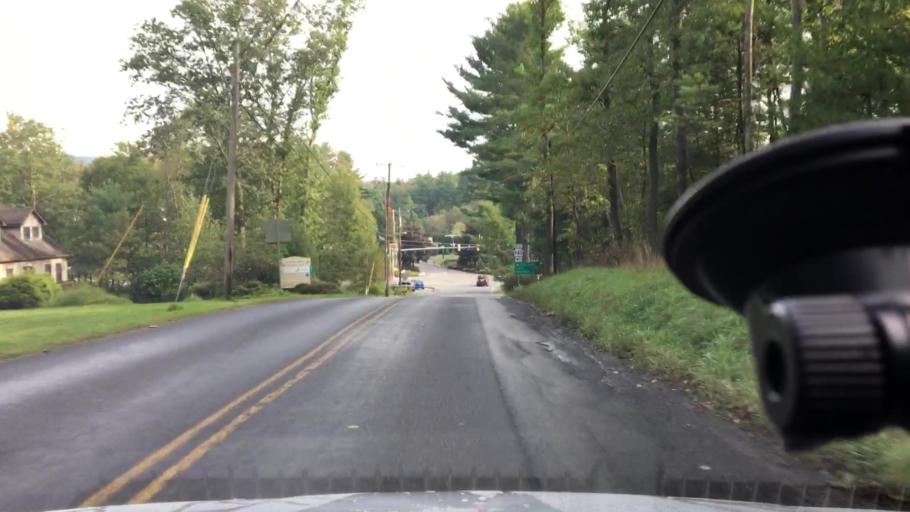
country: US
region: Pennsylvania
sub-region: Monroe County
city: Mount Pocono
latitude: 41.1261
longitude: -75.3109
